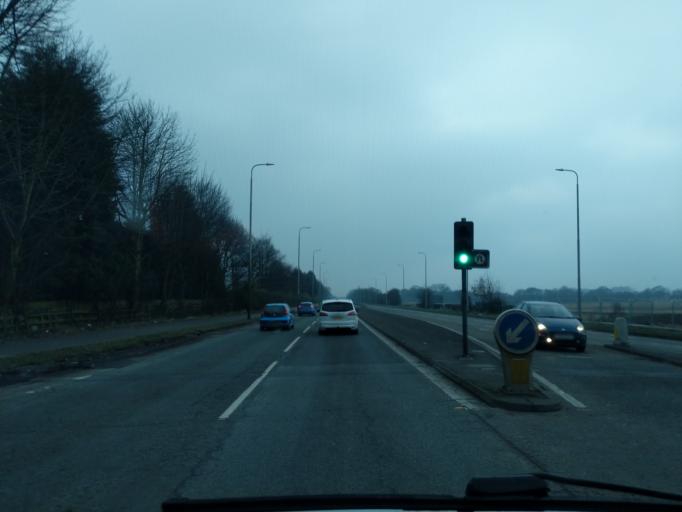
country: GB
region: England
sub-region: St. Helens
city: Haydock
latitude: 53.4725
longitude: -2.6716
